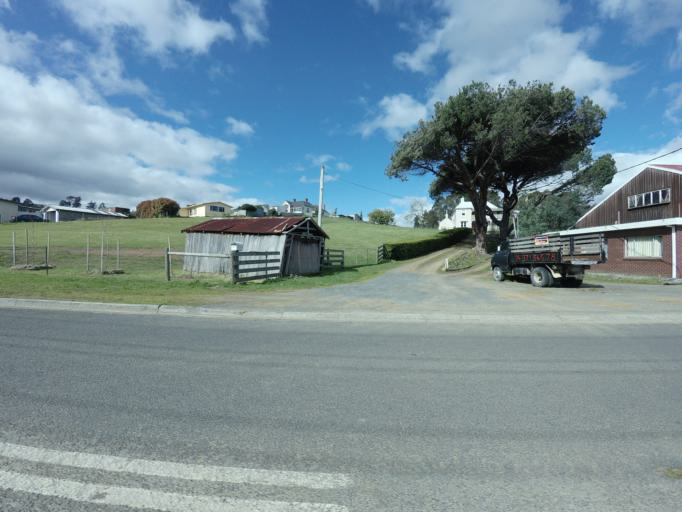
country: AU
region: Tasmania
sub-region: Huon Valley
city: Geeveston
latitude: -43.1658
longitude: 146.9262
